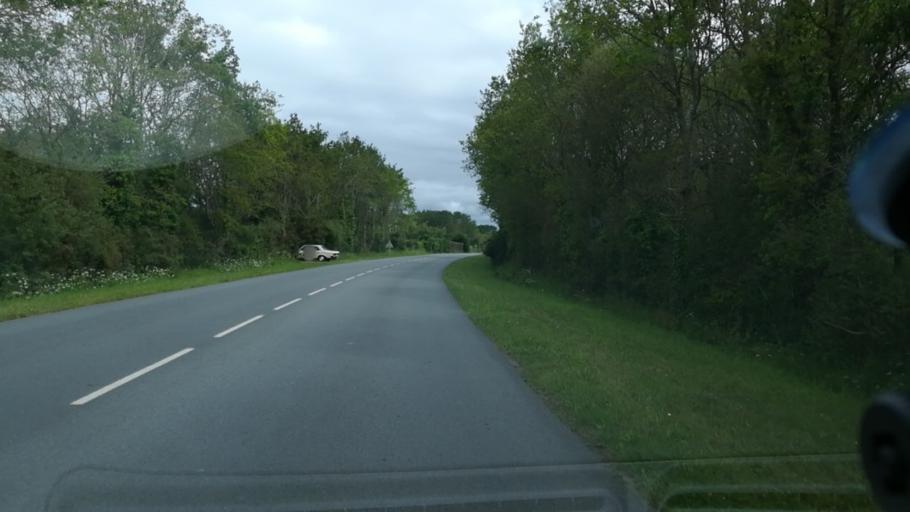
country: FR
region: Brittany
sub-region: Departement du Morbihan
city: Penestin
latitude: 47.4605
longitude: -2.4773
